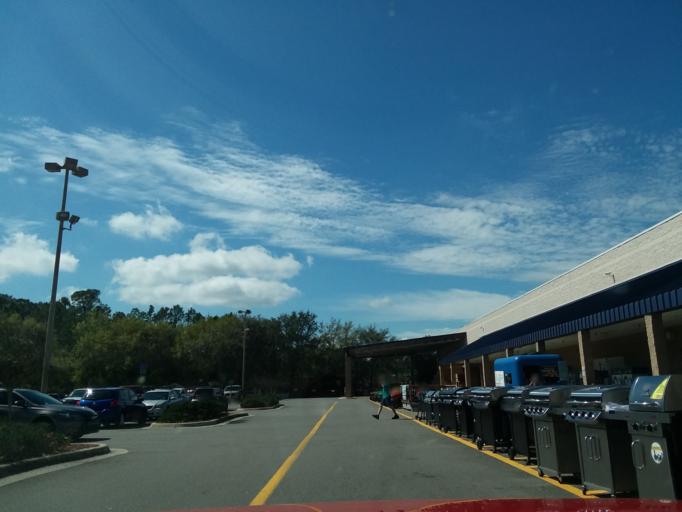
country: US
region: Florida
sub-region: Saint Johns County
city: Fruit Cove
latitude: 30.1670
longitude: -81.6040
